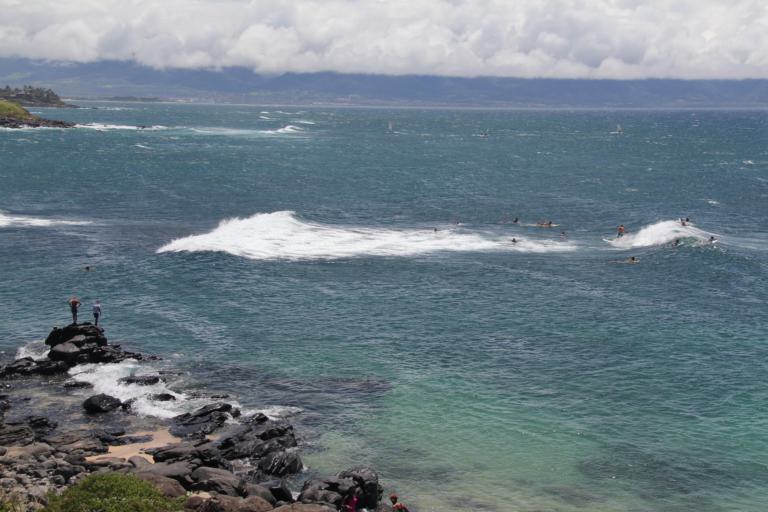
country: US
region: Hawaii
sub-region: Maui County
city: Paia
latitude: 20.9355
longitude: -156.3555
